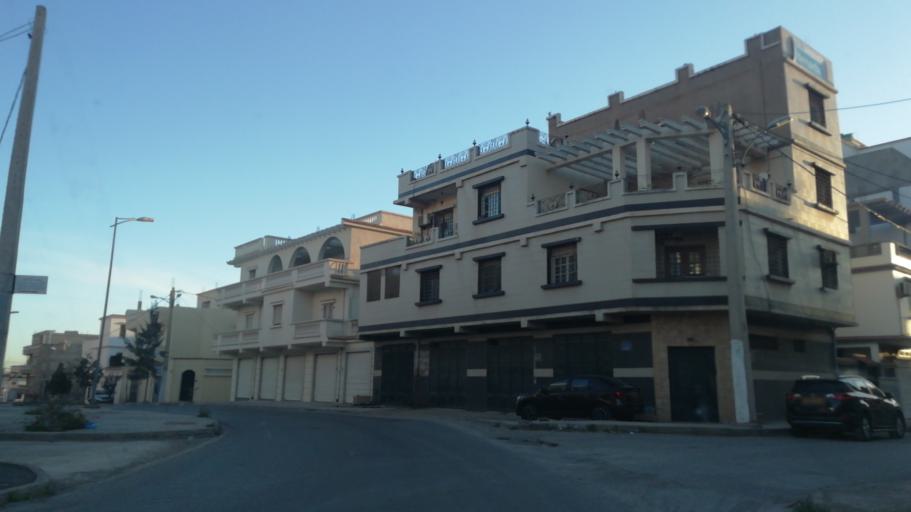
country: DZ
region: Oran
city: Bir el Djir
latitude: 35.7205
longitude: -0.5776
